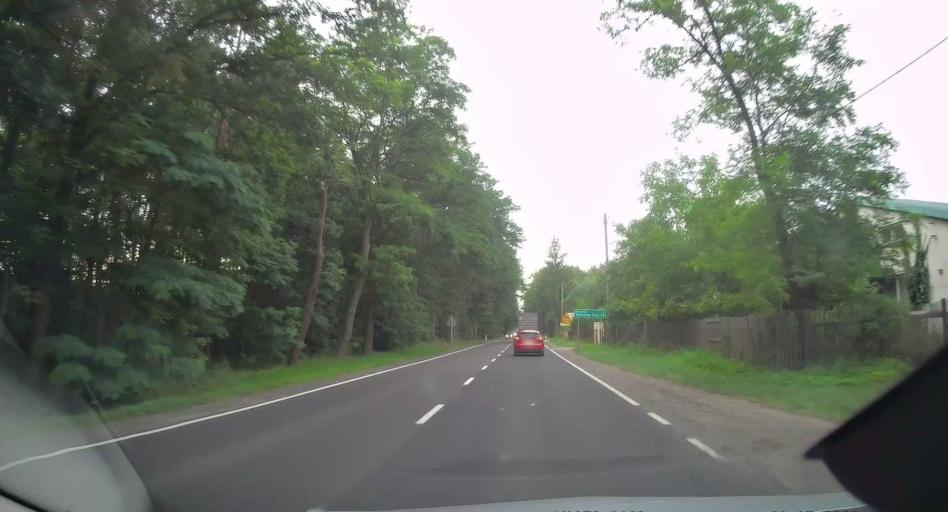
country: PL
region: Lodz Voivodeship
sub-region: Powiat radomszczanski
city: Gomunice
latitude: 51.1628
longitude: 19.4920
